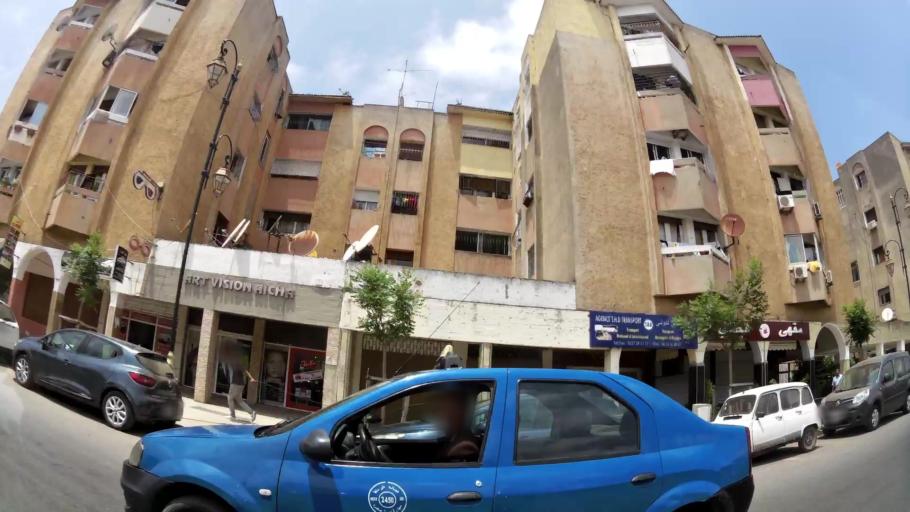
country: MA
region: Rabat-Sale-Zemmour-Zaer
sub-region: Skhirate-Temara
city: Temara
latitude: 33.9716
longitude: -6.8855
